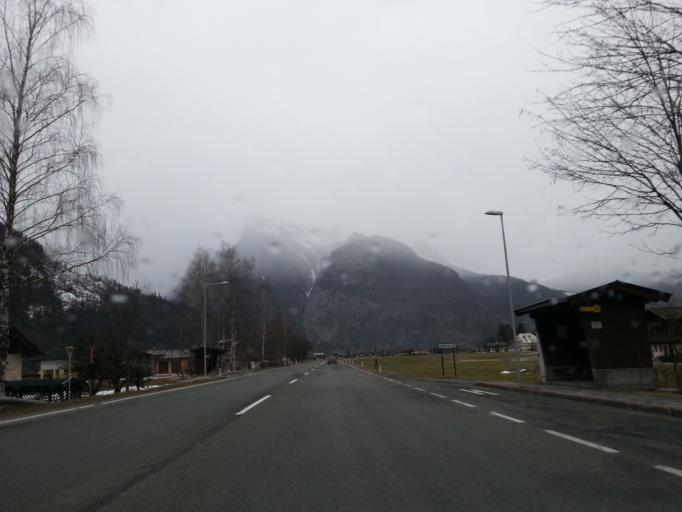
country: AT
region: Salzburg
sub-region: Politischer Bezirk Zell am See
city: Sankt Martin bei Lofer
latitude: 47.5669
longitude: 12.7072
